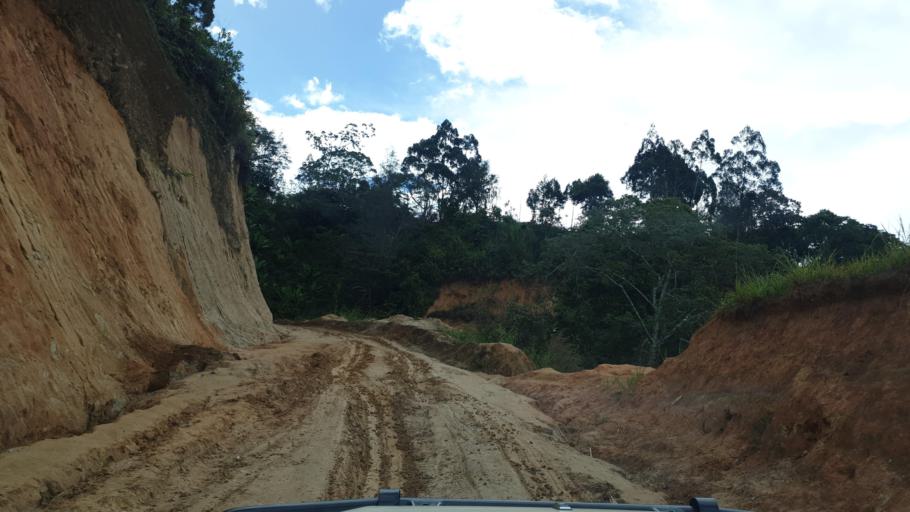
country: PG
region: Eastern Highlands
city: Goroka
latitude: -5.9243
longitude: 145.2636
